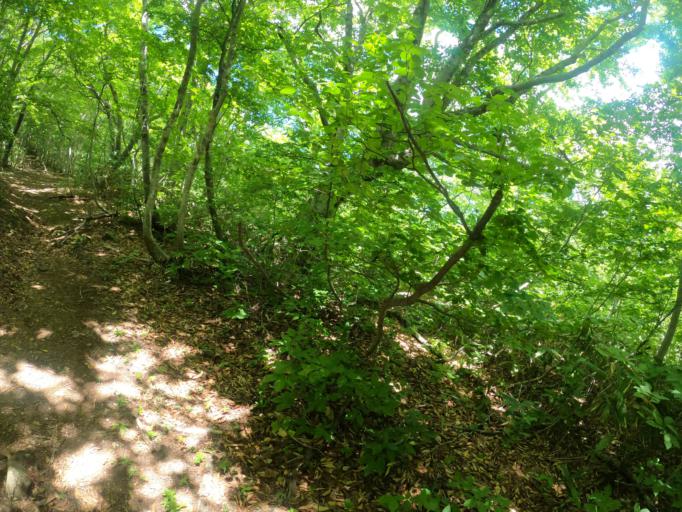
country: JP
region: Iwate
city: Ichinoseki
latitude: 38.9229
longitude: 140.7973
